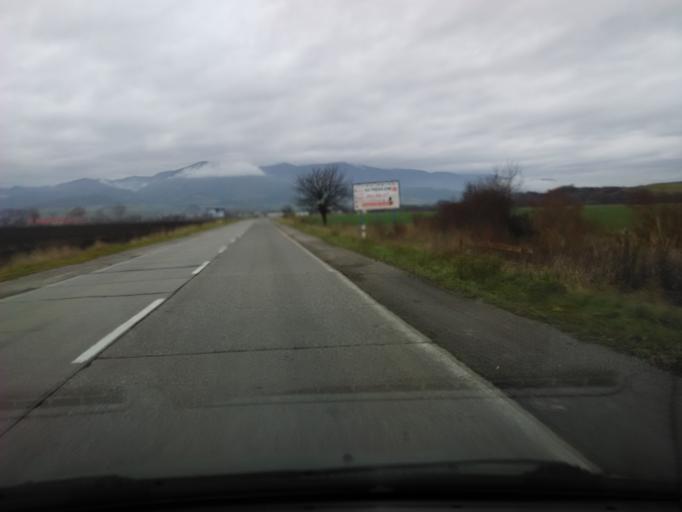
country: SK
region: Zilinsky
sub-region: Okres Martin
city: Martin
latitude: 48.9815
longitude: 18.8998
